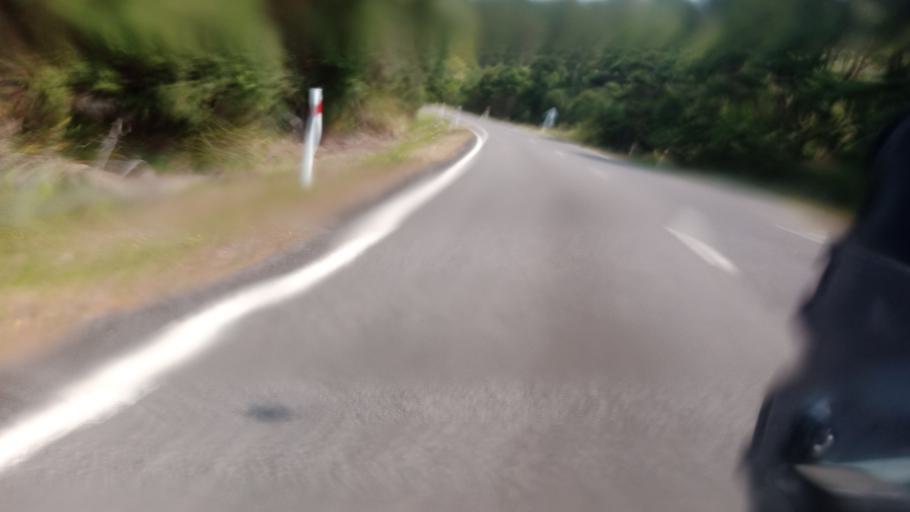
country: NZ
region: Bay of Plenty
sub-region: Opotiki District
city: Opotiki
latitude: -37.5715
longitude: 178.0517
